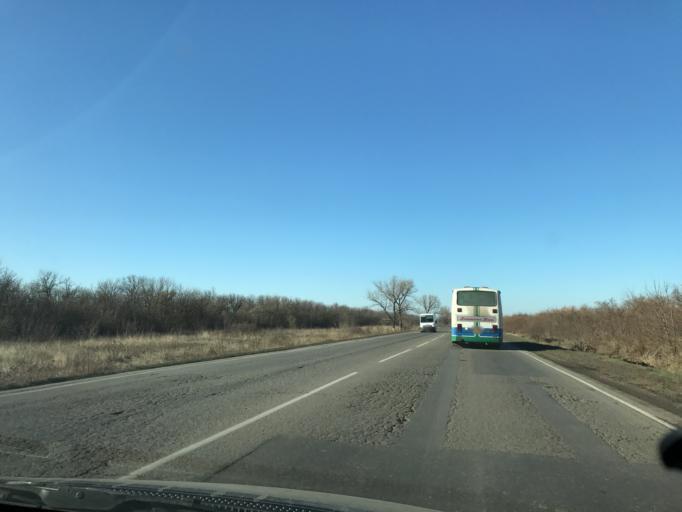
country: RU
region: Rostov
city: Kirovskaya
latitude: 47.0146
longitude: 39.9193
